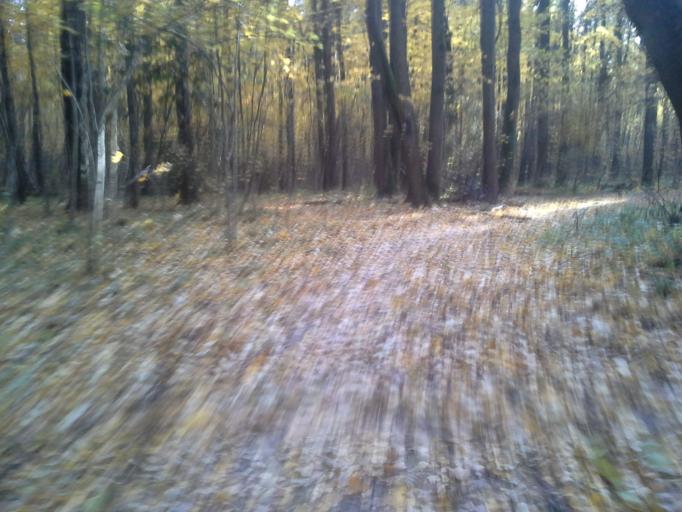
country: RU
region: Moskovskaya
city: Kommunarka
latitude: 55.5679
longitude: 37.5292
